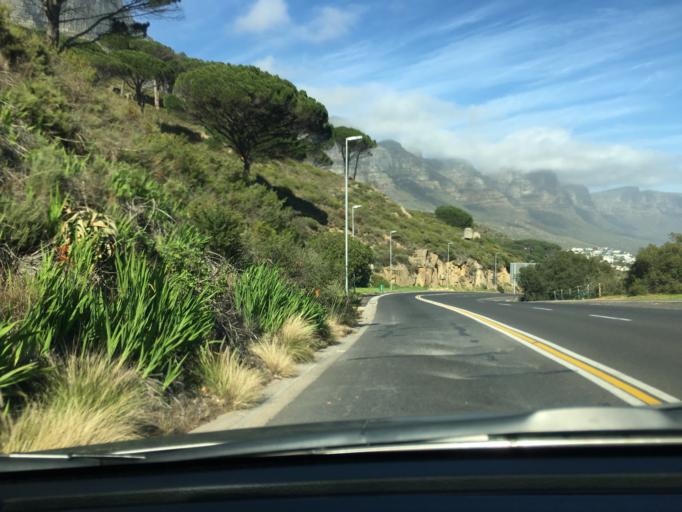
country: ZA
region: Western Cape
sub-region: City of Cape Town
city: Cape Town
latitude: -33.9432
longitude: 18.3932
